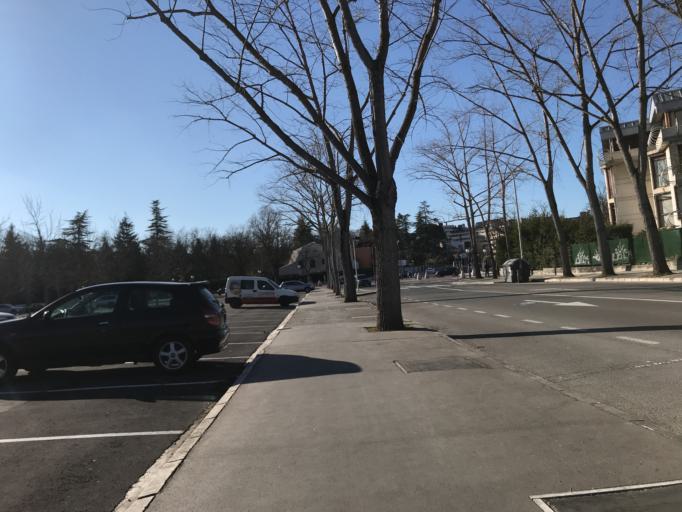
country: ES
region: Basque Country
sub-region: Provincia de Alava
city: Gasteiz / Vitoria
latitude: 42.8383
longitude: -2.6873
